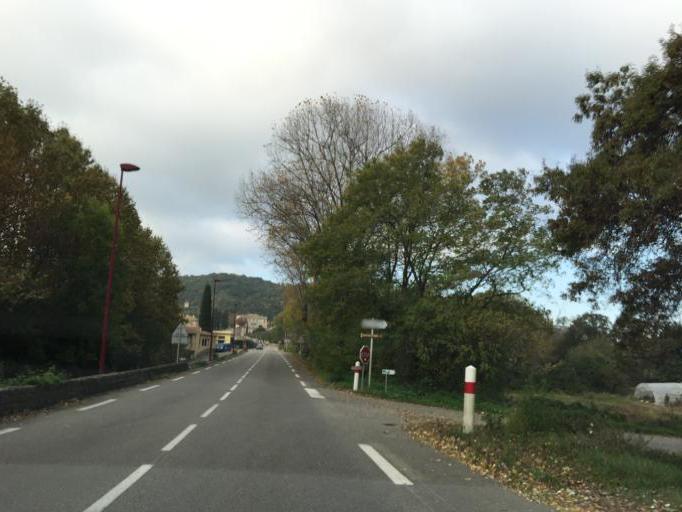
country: FR
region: Rhone-Alpes
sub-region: Departement de l'Ardeche
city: Viviers
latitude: 44.4815
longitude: 4.6970
